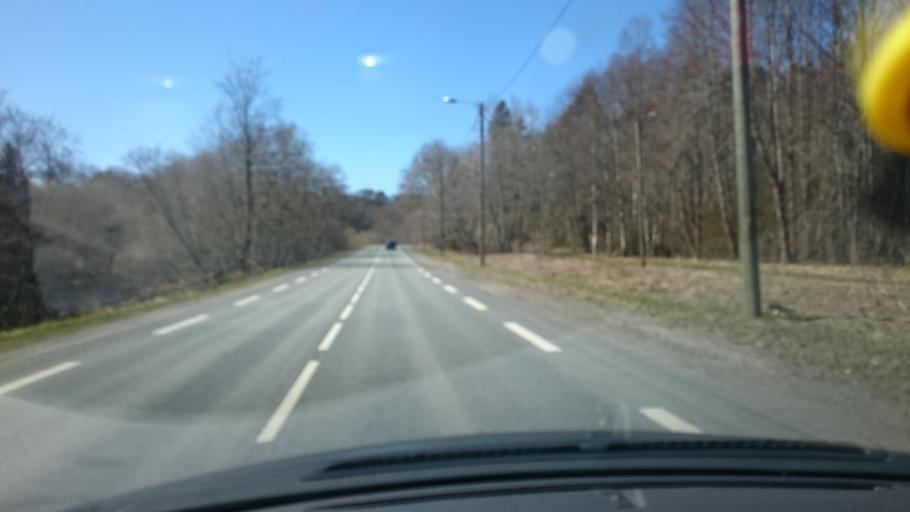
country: EE
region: Harju
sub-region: Tallinna linn
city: Kose
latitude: 59.4603
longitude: 24.8619
